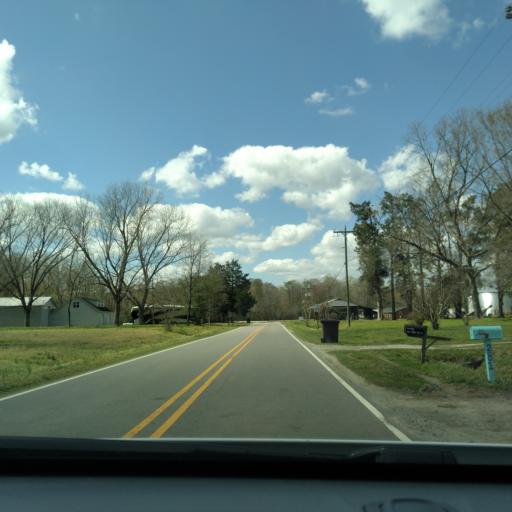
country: US
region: North Carolina
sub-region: Washington County
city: Plymouth
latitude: 35.8417
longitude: -76.7266
